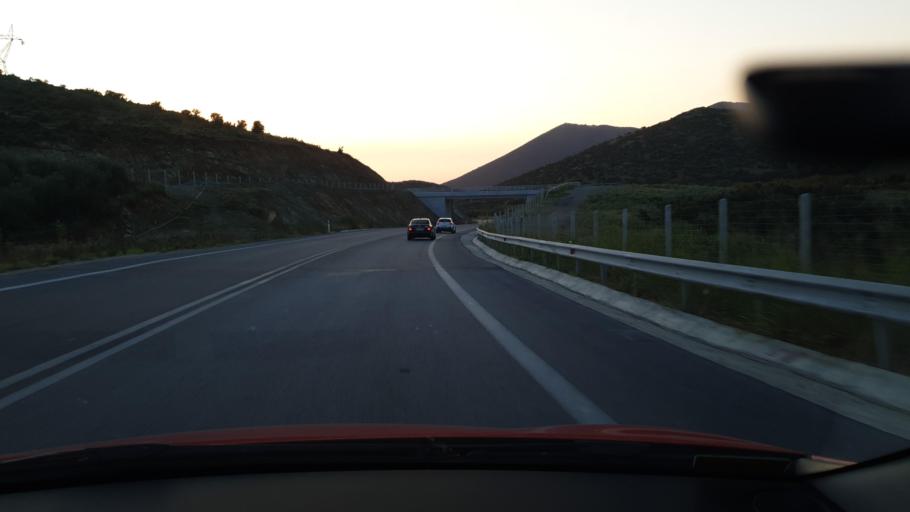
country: GR
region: Central Macedonia
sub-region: Nomos Chalkidikis
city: Galatista
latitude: 40.4651
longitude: 23.2128
